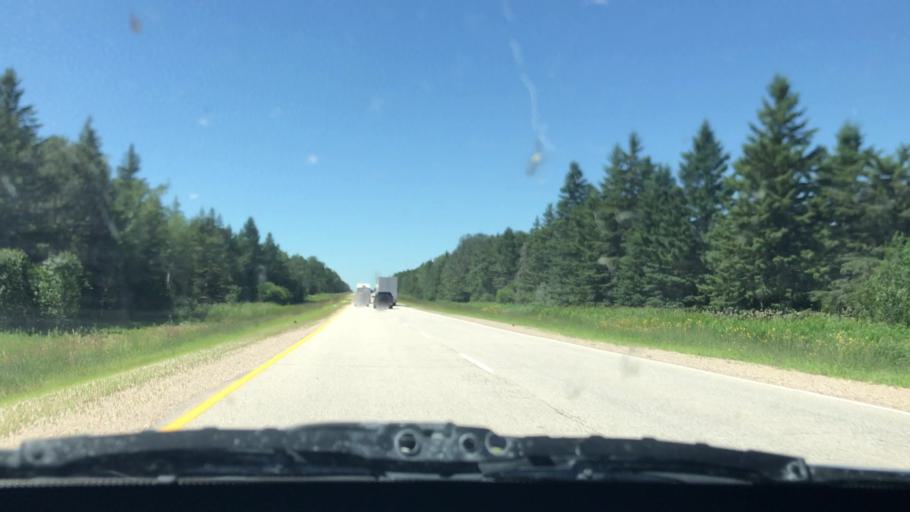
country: CA
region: Manitoba
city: La Broquerie
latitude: 49.6572
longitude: -96.1913
